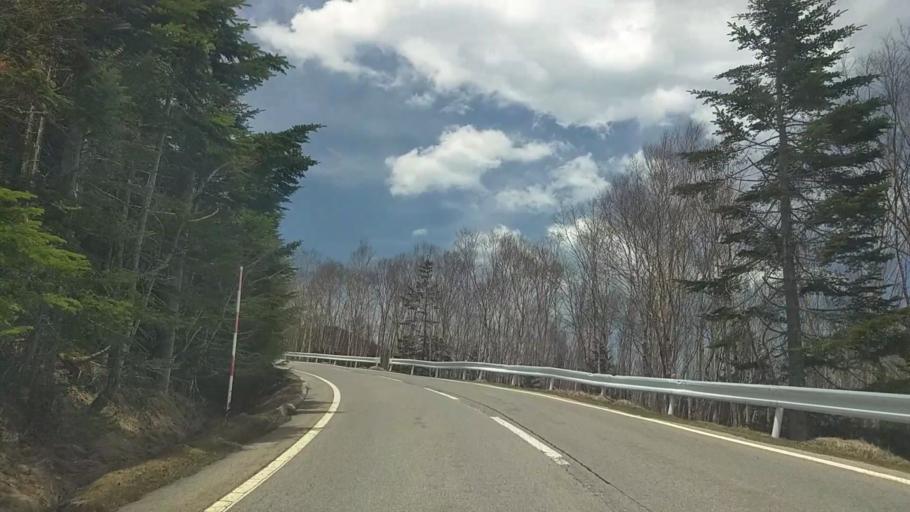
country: JP
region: Nagano
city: Saku
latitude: 36.0574
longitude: 138.3544
